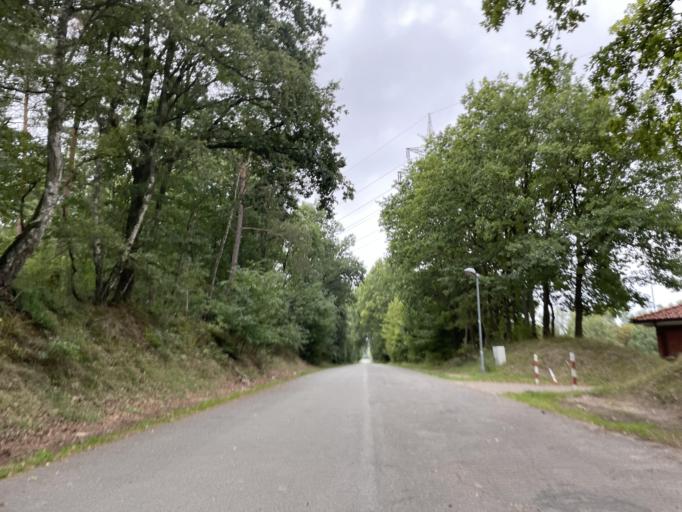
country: DE
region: Lower Saxony
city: Wendisch Evern
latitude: 53.2092
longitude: 10.4799
